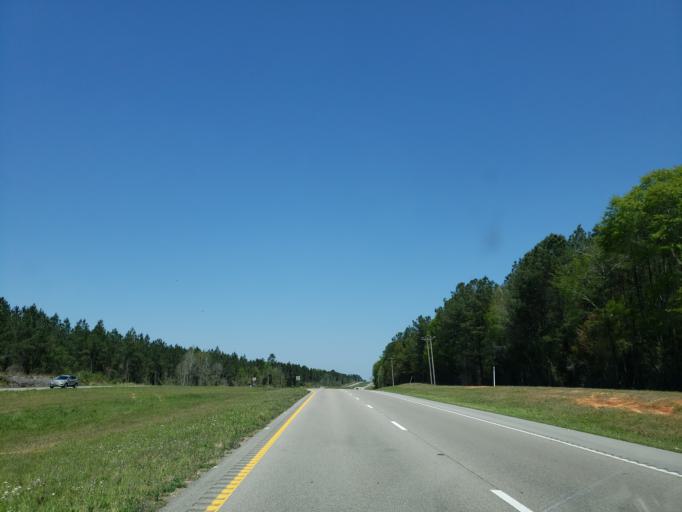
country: US
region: Mississippi
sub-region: Stone County
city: Wiggins
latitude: 31.0049
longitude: -89.2014
